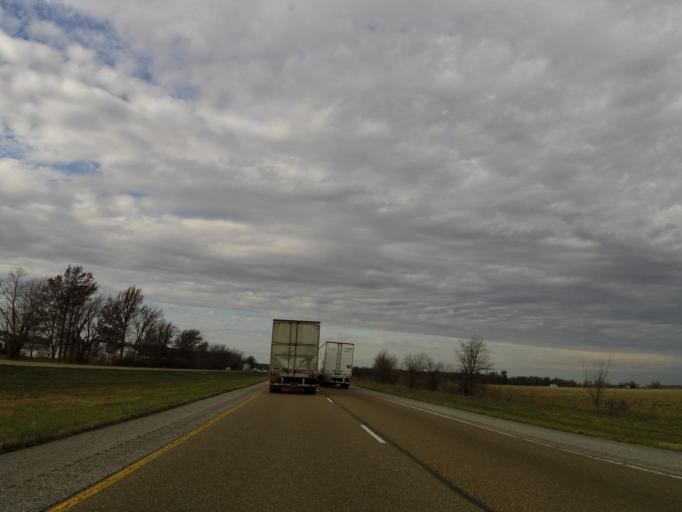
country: US
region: Illinois
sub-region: Washington County
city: Nashville
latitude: 38.3914
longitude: -89.2873
